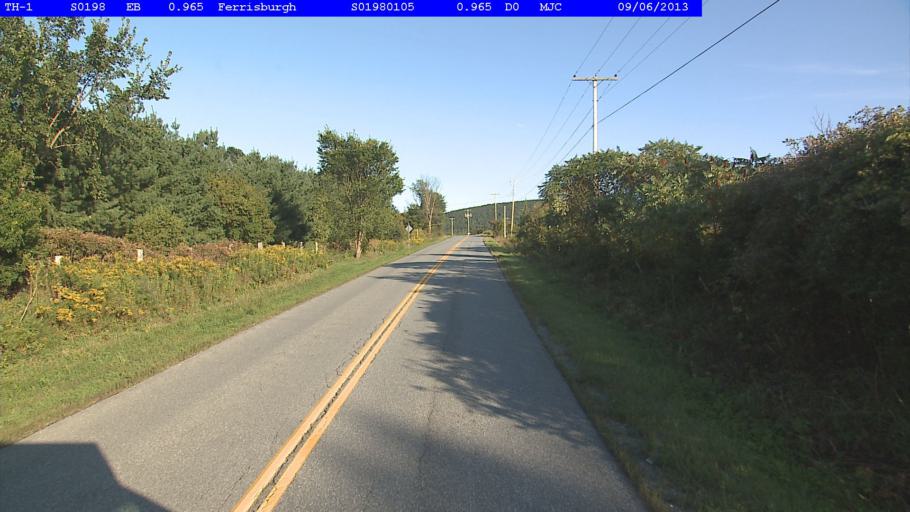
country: US
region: Vermont
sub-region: Addison County
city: Vergennes
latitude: 44.2588
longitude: -73.2091
